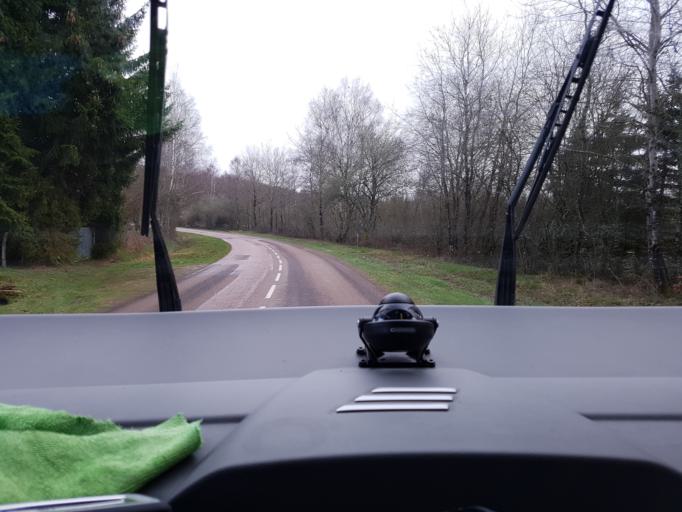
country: FR
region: Bourgogne
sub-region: Departement de la Cote-d'Or
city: Saulieu
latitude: 47.2755
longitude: 4.0233
